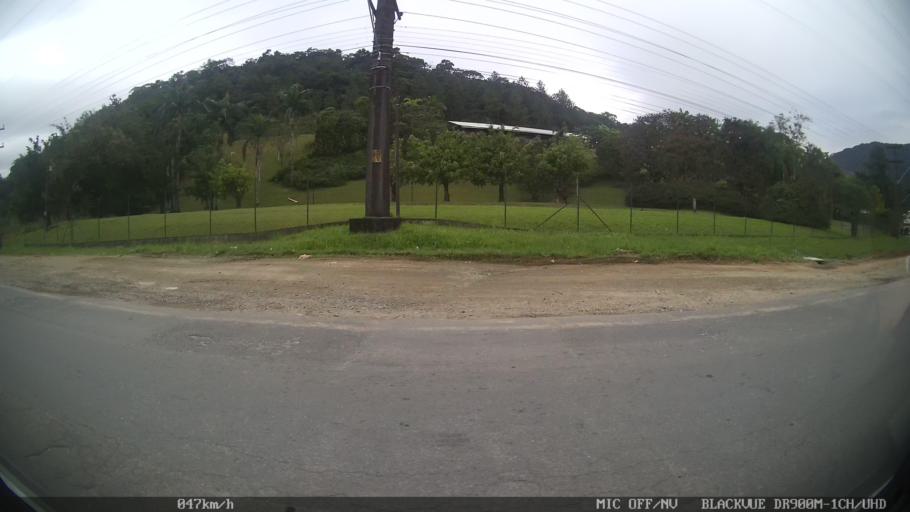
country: BR
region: Santa Catarina
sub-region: Joinville
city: Joinville
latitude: -26.2304
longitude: -48.9143
